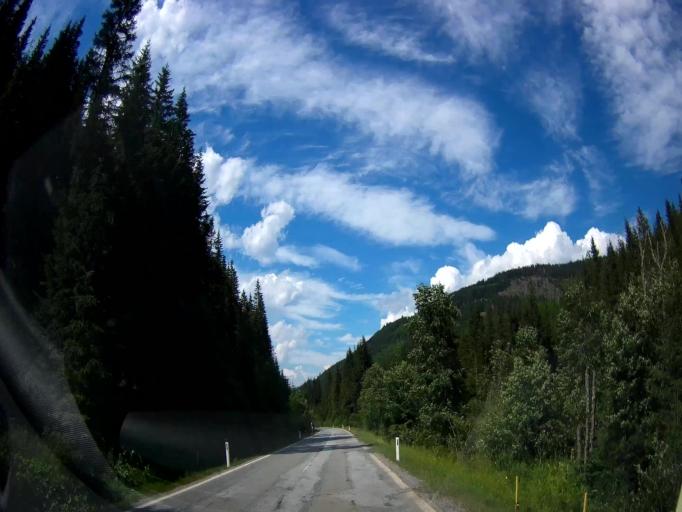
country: AT
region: Styria
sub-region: Politischer Bezirk Murau
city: Stadl an der Mur
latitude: 46.9987
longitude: 14.0145
